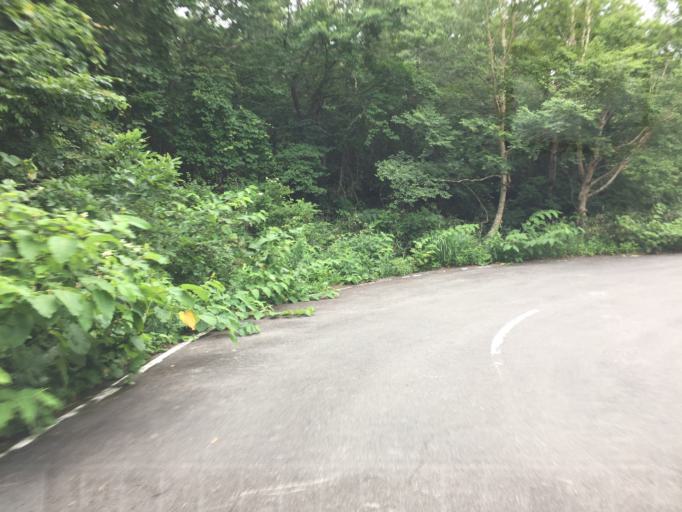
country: JP
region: Fukushima
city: Nihommatsu
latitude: 37.6581
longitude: 140.3018
